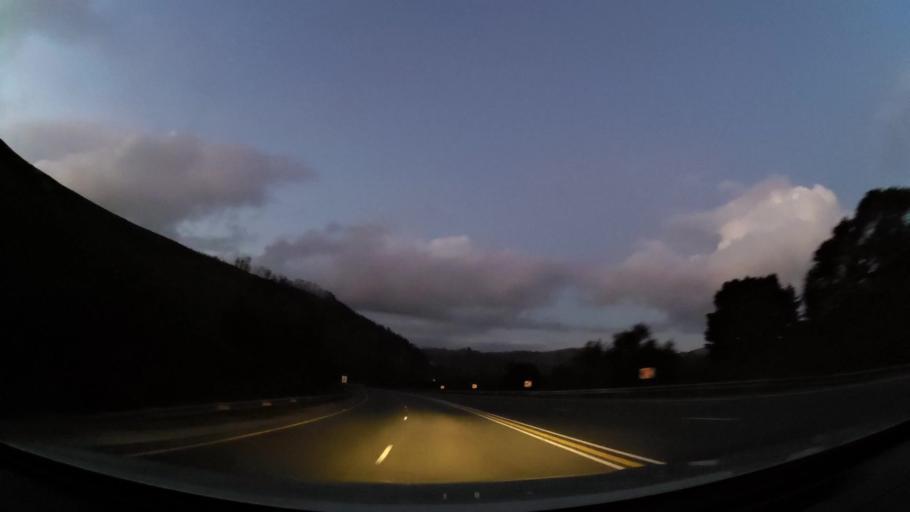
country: ZA
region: Western Cape
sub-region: Eden District Municipality
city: Knysna
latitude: -34.0390
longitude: 22.9244
